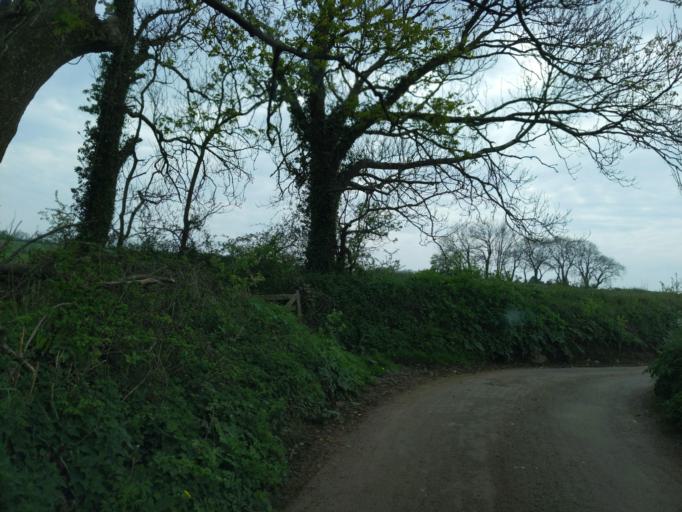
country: GB
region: England
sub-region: Devon
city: Yealmpton
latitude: 50.3653
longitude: -4.0240
